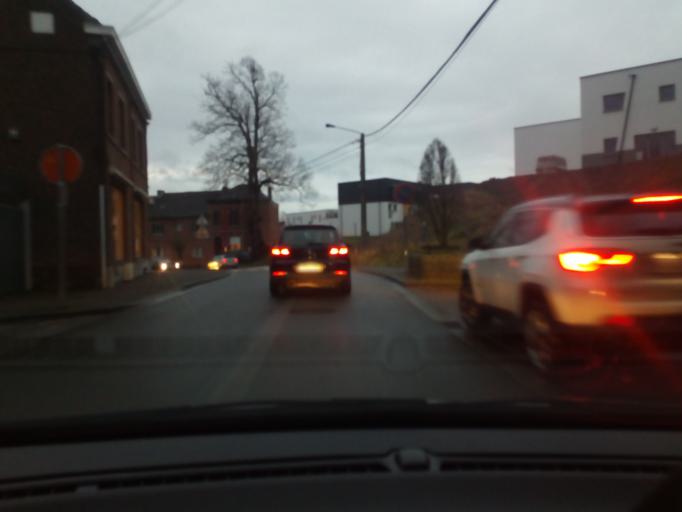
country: BE
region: Wallonia
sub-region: Province du Hainaut
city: Estinnes-au-Val
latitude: 50.4565
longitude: 4.0946
